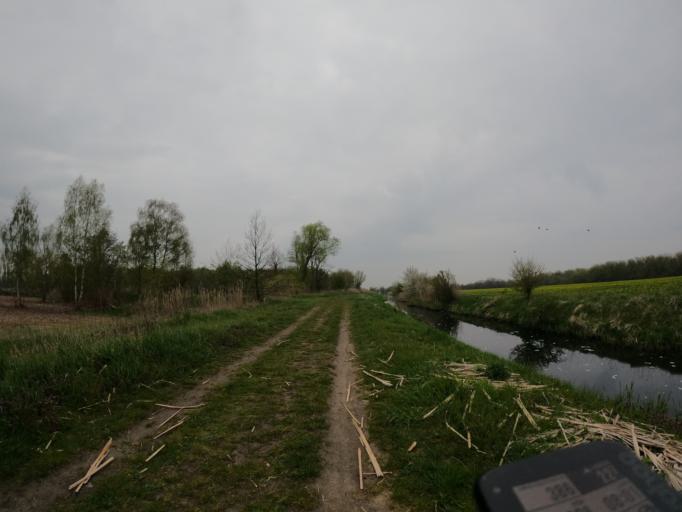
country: DE
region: Berlin
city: Gropiusstadt
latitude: 52.3779
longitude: 13.4596
